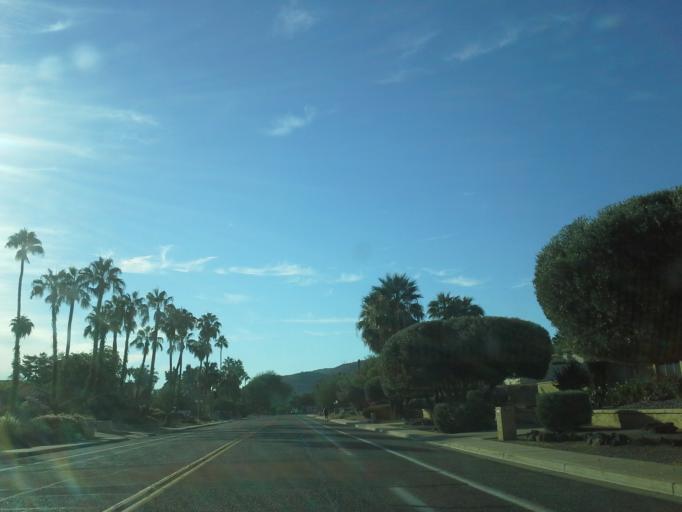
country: US
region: Arizona
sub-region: Maricopa County
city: Glendale
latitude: 33.6173
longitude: -112.0860
